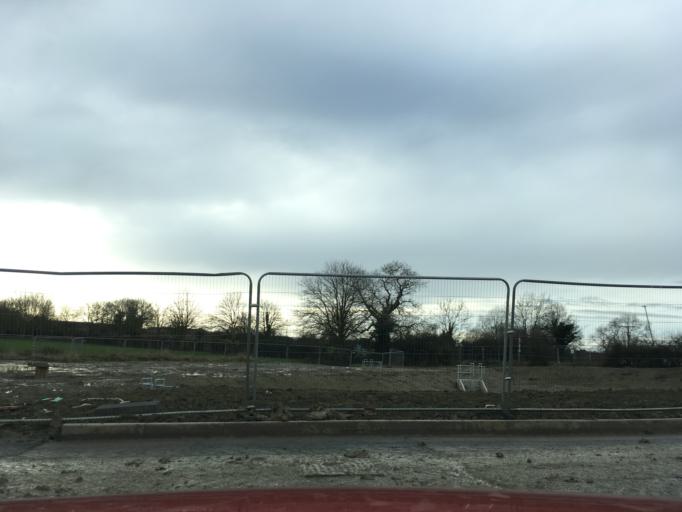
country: GB
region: England
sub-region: Worcestershire
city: Bredon
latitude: 51.9989
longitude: -2.0929
